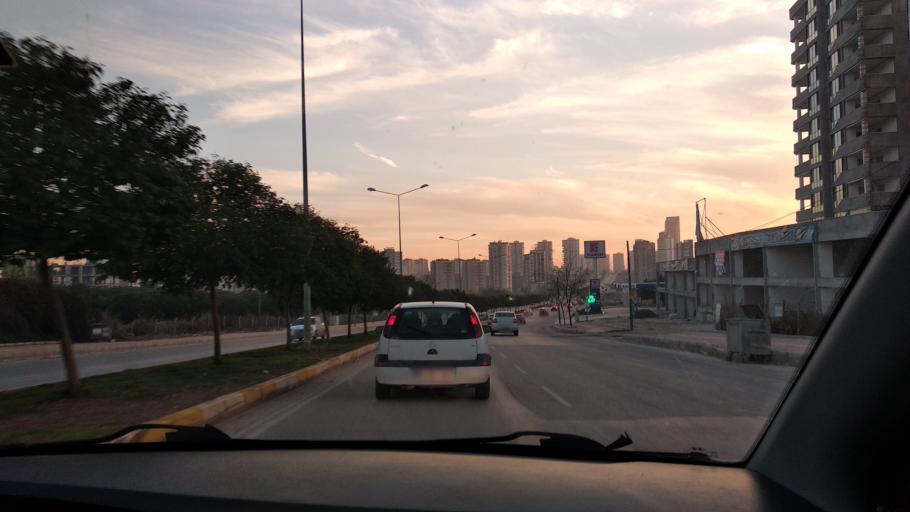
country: TR
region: Mersin
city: Mercin
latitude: 36.8168
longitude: 34.5960
